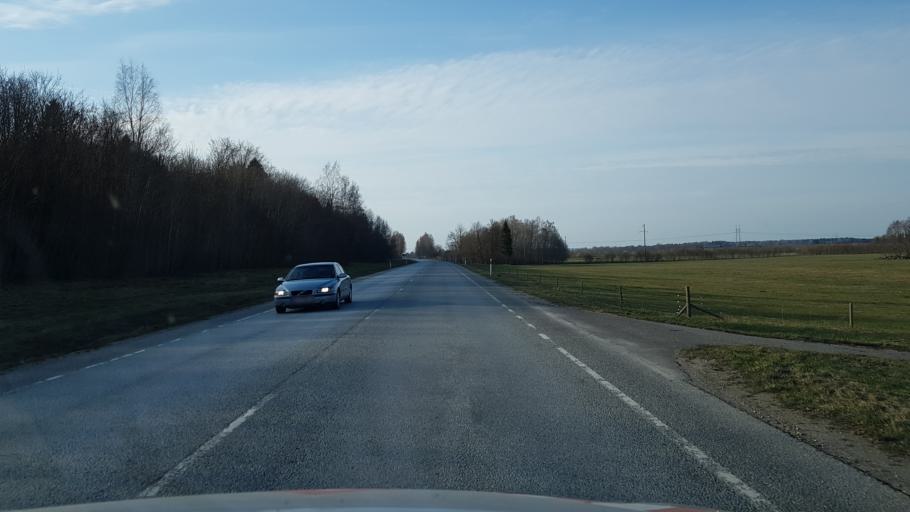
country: EE
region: Laeaene-Virumaa
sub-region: Haljala vald
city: Haljala
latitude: 59.3979
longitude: 26.3074
